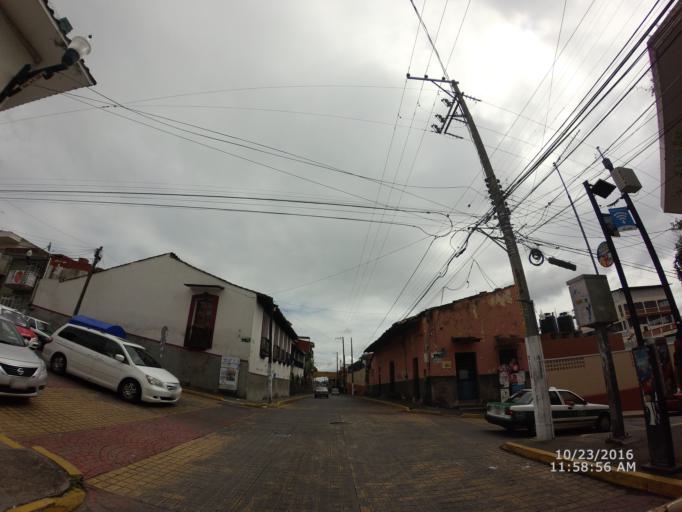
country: MX
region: Veracruz
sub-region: Xalapa
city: Xalapa de Enriquez
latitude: 19.5329
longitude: -96.9194
